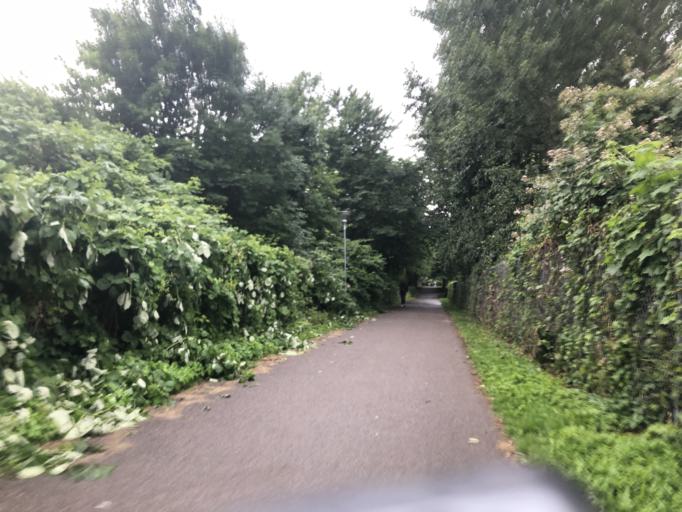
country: DK
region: Capital Region
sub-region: Gladsaxe Municipality
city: Buddinge
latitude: 55.7476
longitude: 12.4924
